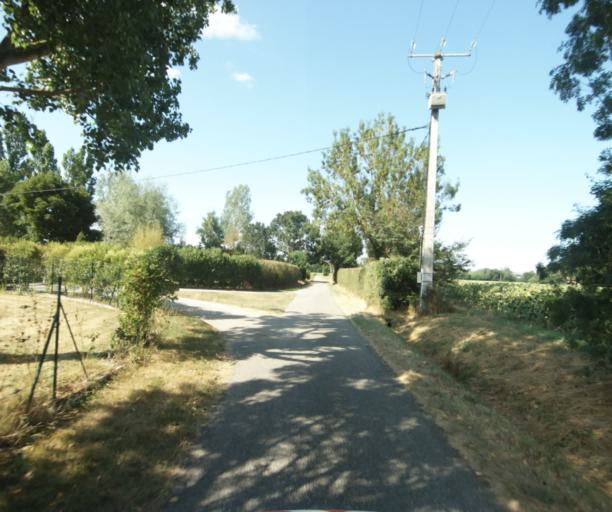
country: FR
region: Midi-Pyrenees
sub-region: Departement de la Haute-Garonne
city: Revel
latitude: 43.5141
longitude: 1.9850
